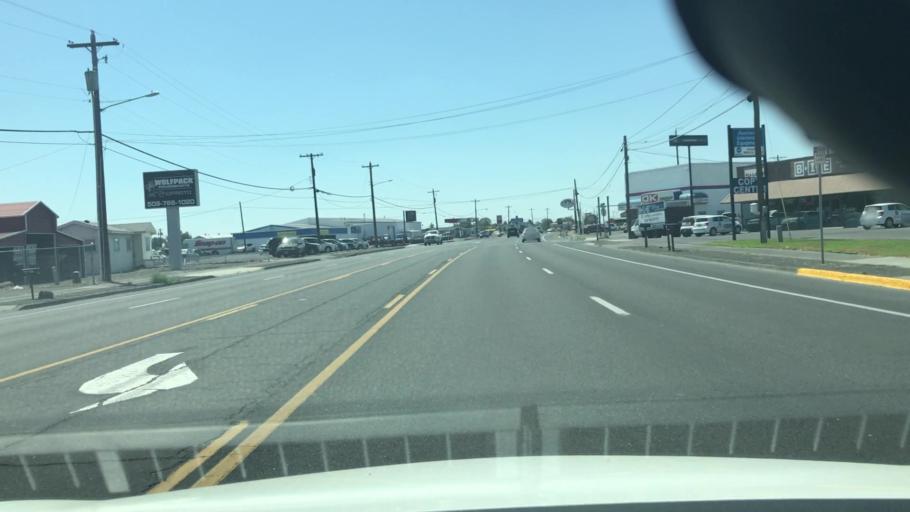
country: US
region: Washington
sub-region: Grant County
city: Moses Lake
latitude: 47.1158
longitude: -119.2965
